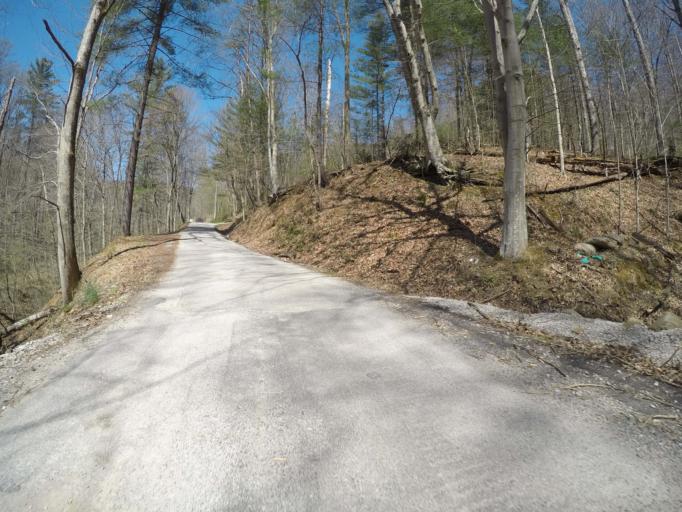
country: US
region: West Virginia
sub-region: Kanawha County
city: Charleston
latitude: 38.4063
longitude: -81.5888
